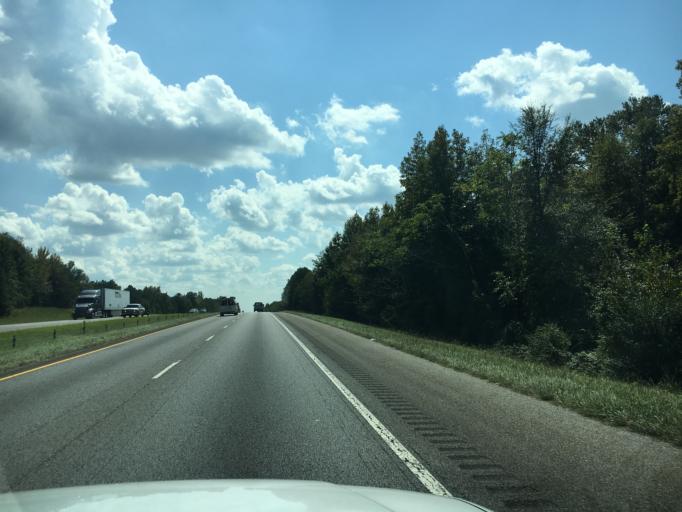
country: US
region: South Carolina
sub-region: Spartanburg County
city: Roebuck
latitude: 34.9053
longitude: -81.9912
